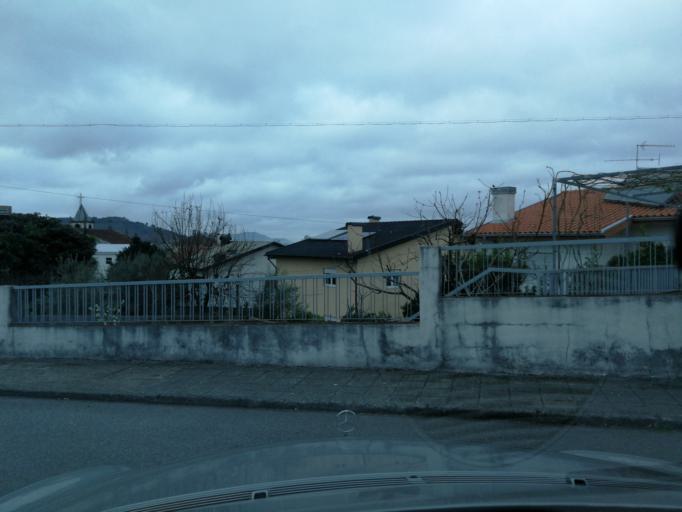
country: PT
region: Braga
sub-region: Braga
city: Braga
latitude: 41.5456
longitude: -8.3947
